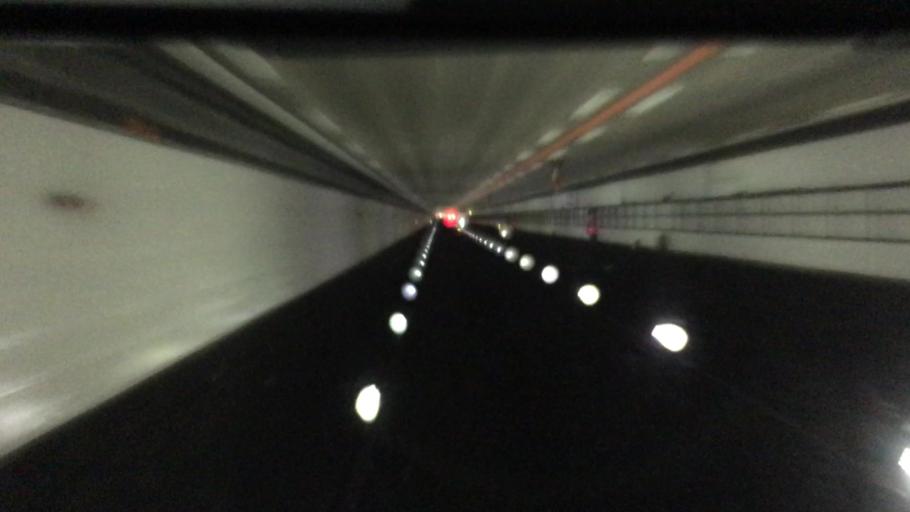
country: JP
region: Yamaguchi
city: Ogori-shimogo
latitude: 34.1065
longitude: 131.4491
